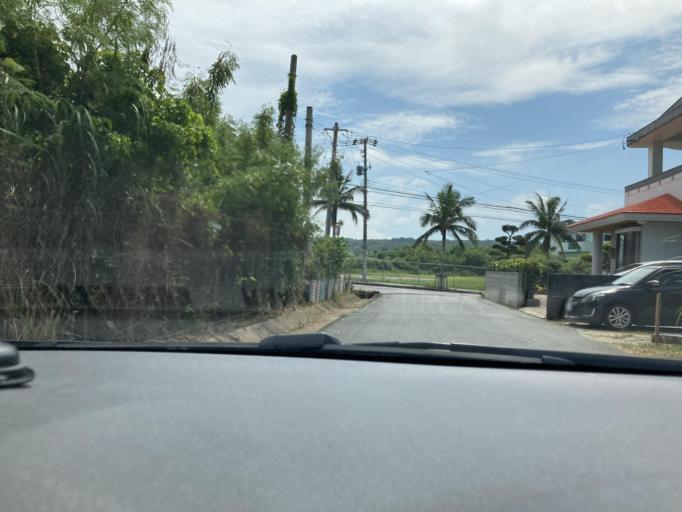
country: JP
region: Okinawa
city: Ishikawa
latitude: 26.4394
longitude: 127.7727
